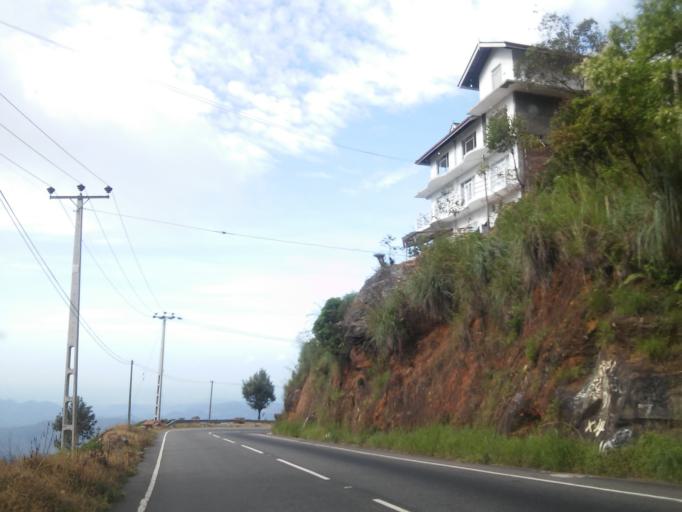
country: LK
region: Uva
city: Haputale
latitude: 6.7630
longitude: 80.9530
